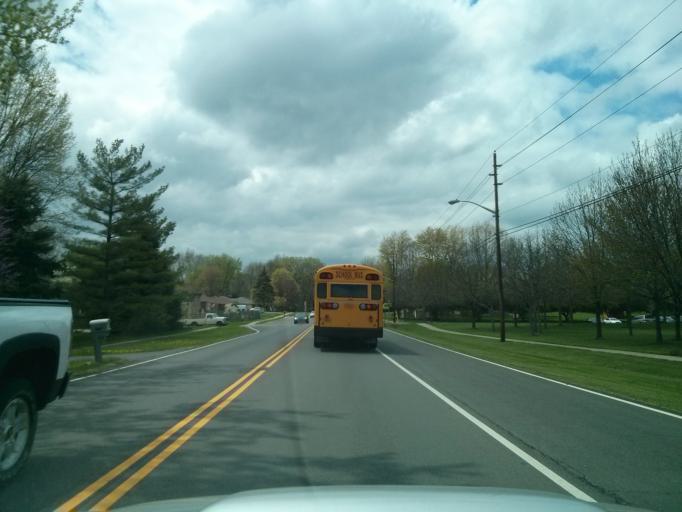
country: US
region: Indiana
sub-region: Hamilton County
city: Carmel
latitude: 39.9713
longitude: -86.1003
